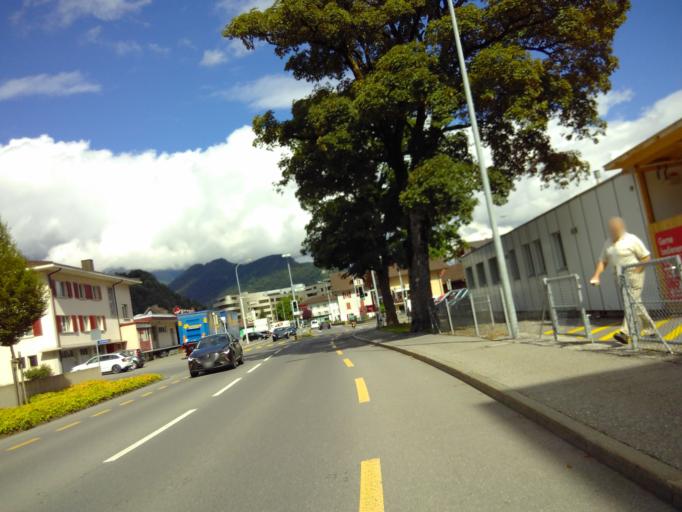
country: CH
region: Nidwalden
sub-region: Nidwalden
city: Stans
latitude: 46.9627
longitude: 8.3593
